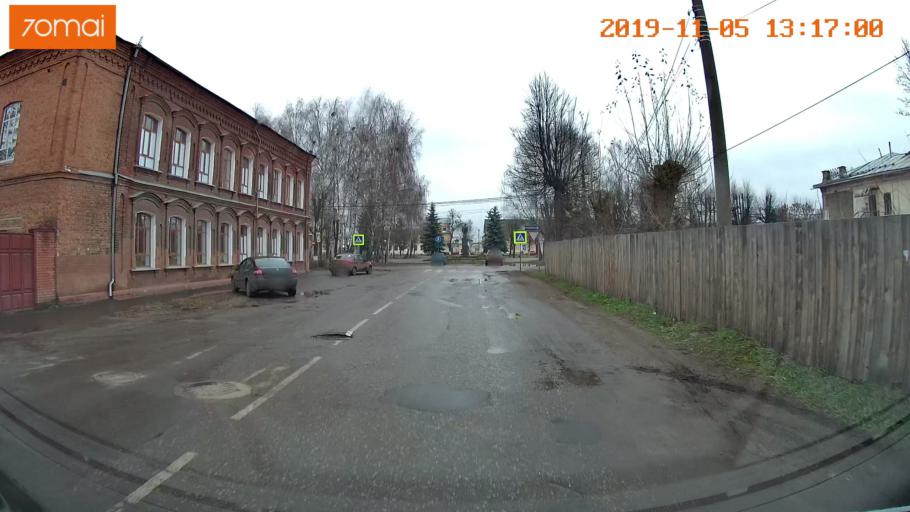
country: RU
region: Ivanovo
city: Shuya
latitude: 56.8539
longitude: 41.3774
